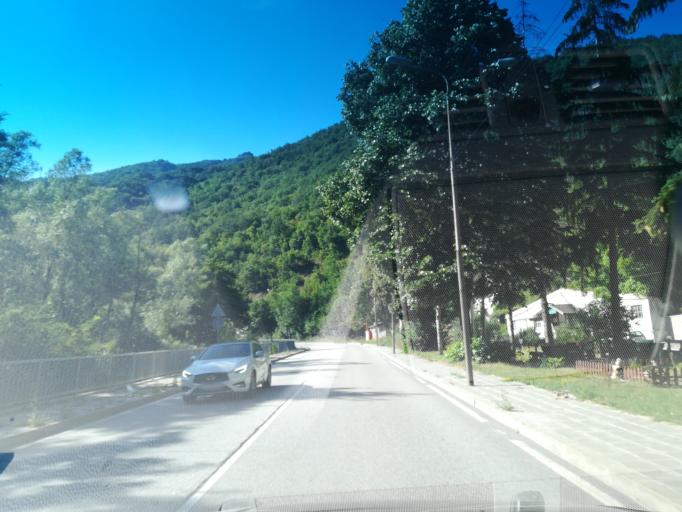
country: BG
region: Plovdiv
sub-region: Obshtina Luki
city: Luki
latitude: 41.8994
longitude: 24.7407
